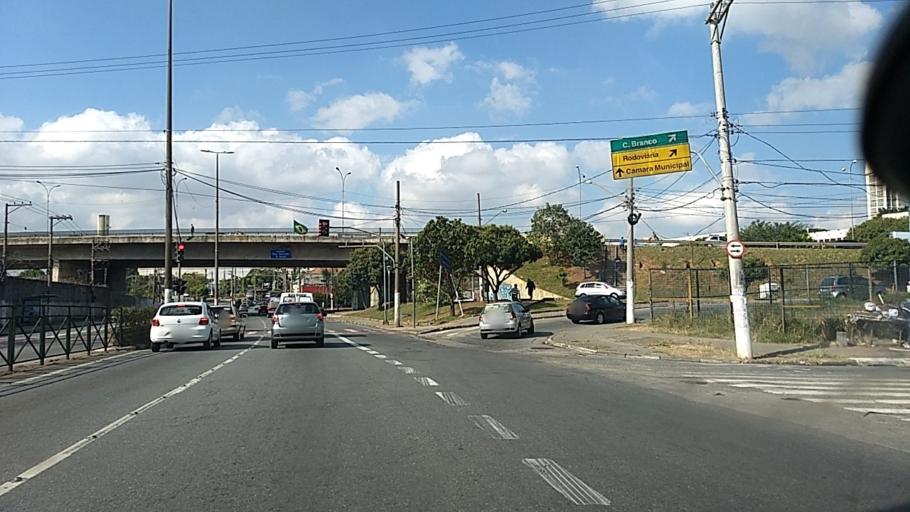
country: BR
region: Sao Paulo
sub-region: Osasco
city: Osasco
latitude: -23.5266
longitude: -46.7924
